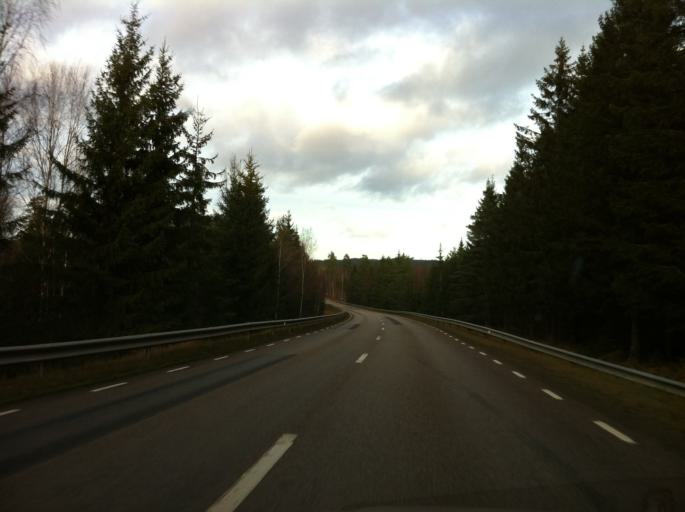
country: SE
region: Kronoberg
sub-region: Uppvidinge Kommun
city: Aseda
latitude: 57.1765
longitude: 15.4956
